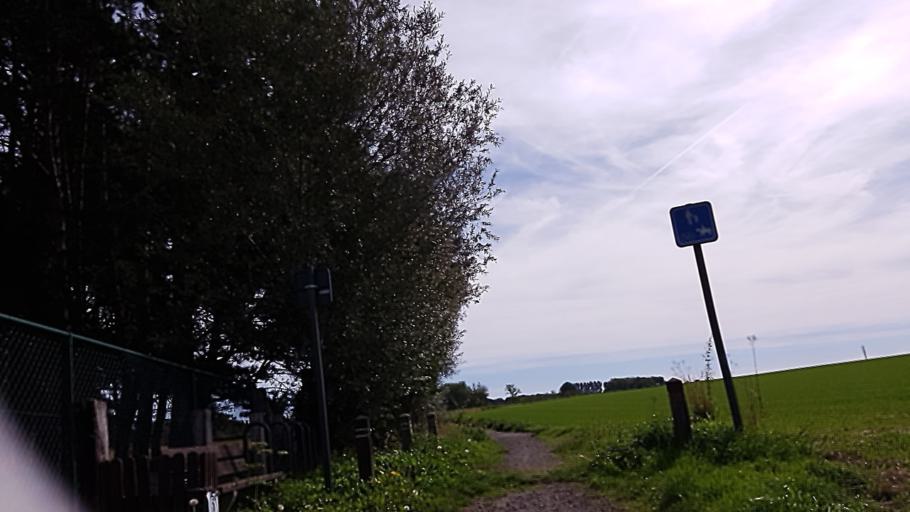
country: BE
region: Wallonia
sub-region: Province du Brabant Wallon
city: Beauvechain
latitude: 50.7771
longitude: 4.7264
